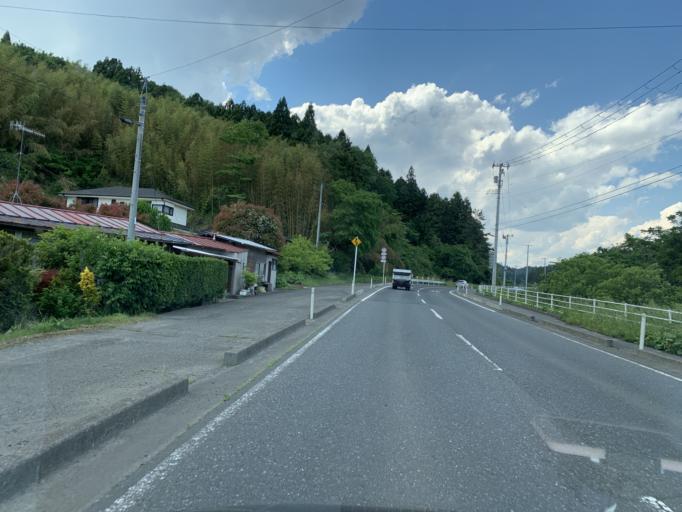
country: JP
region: Miyagi
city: Wakuya
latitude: 38.5514
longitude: 141.1402
